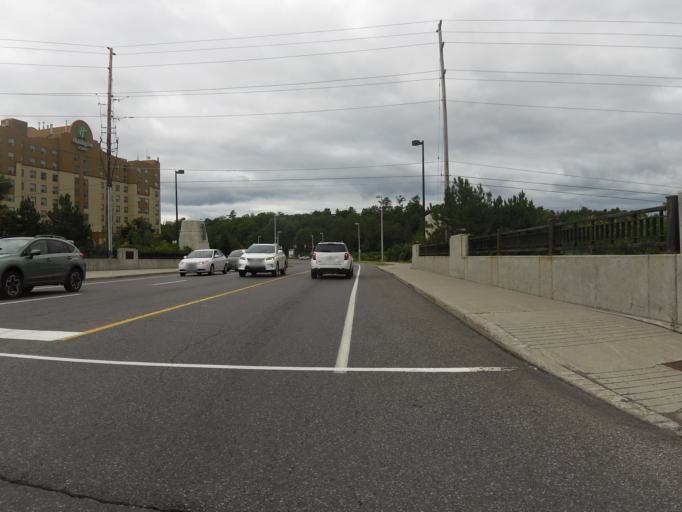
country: CA
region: Ontario
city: Bells Corners
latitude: 45.3116
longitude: -75.9031
